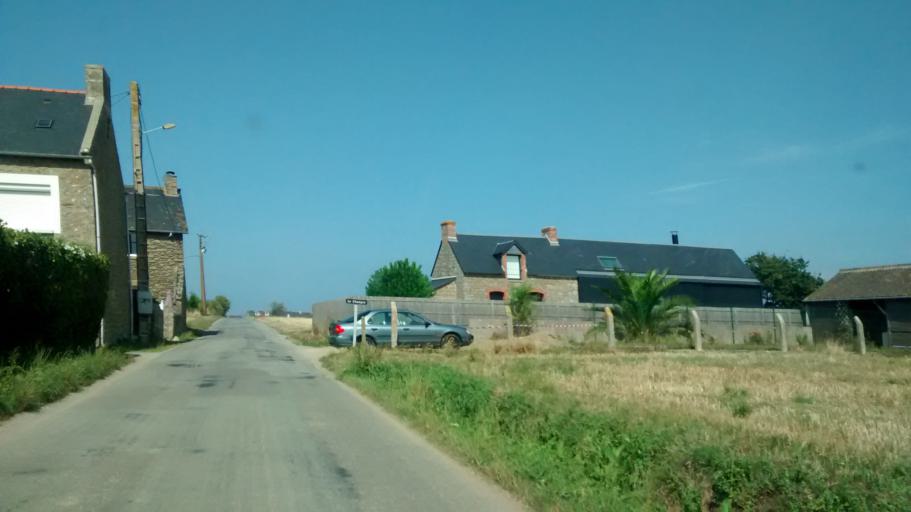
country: FR
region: Brittany
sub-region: Departement d'Ille-et-Vilaine
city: Saint-Coulomb
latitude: 48.6786
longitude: -1.8983
